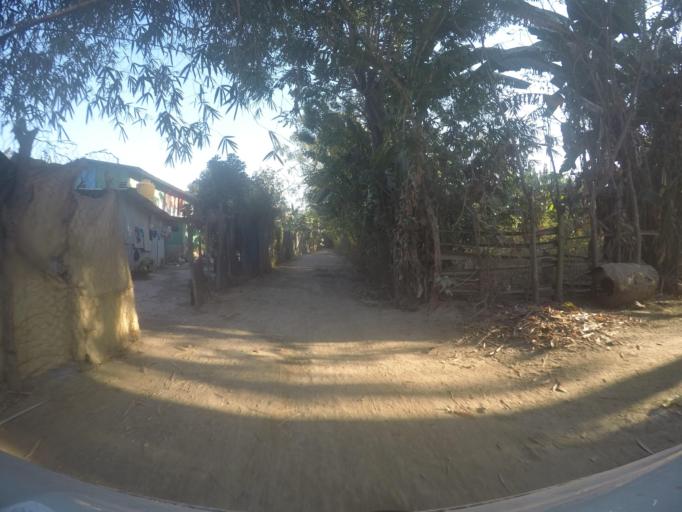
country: ID
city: Metinaro
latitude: -8.5471
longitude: 125.6666
